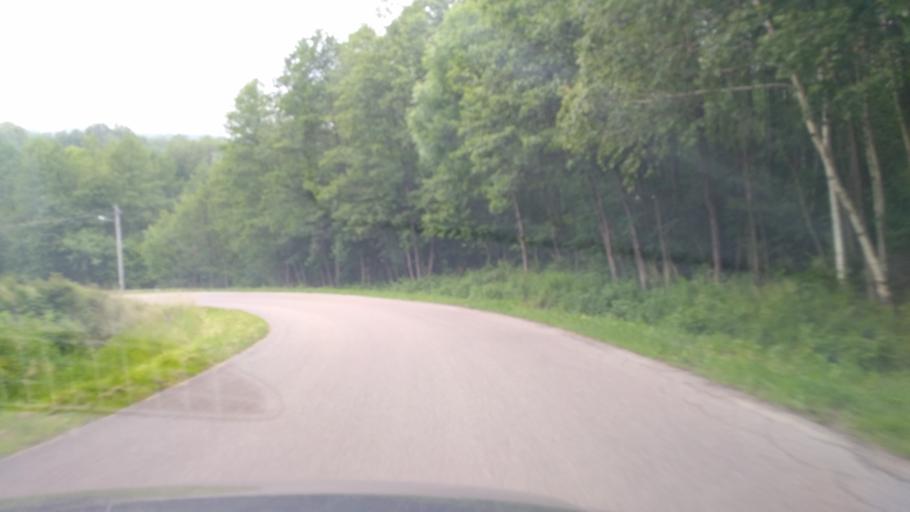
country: PL
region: Subcarpathian Voivodeship
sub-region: Powiat ropczycko-sedziszowski
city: Zagorzyce
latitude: 49.9927
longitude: 21.6993
